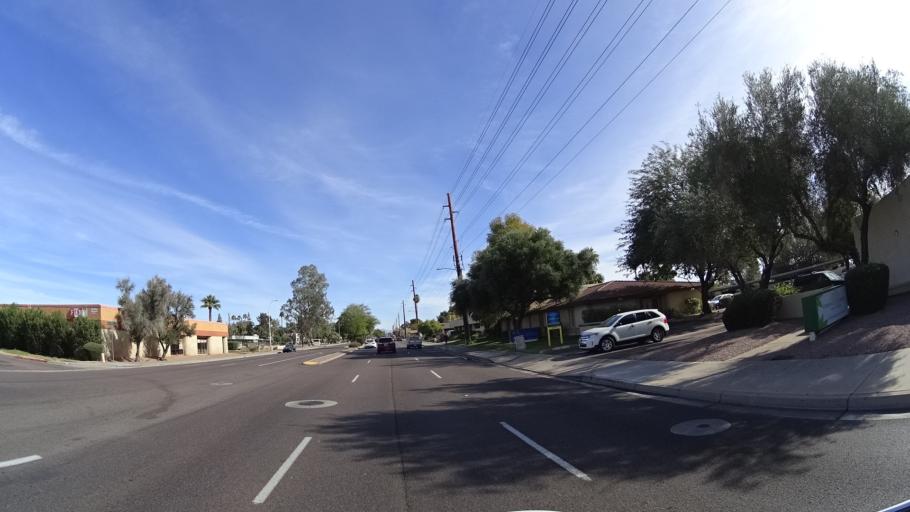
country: US
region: Arizona
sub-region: Maricopa County
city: Tempe
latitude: 33.4074
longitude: -111.9029
